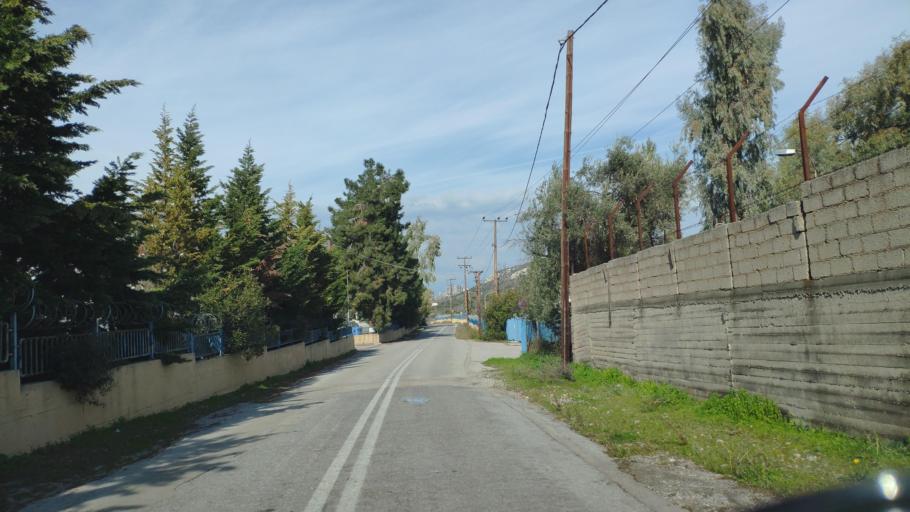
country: GR
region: Central Greece
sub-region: Nomos Evvoias
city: Vathi
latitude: 38.4177
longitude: 23.5912
